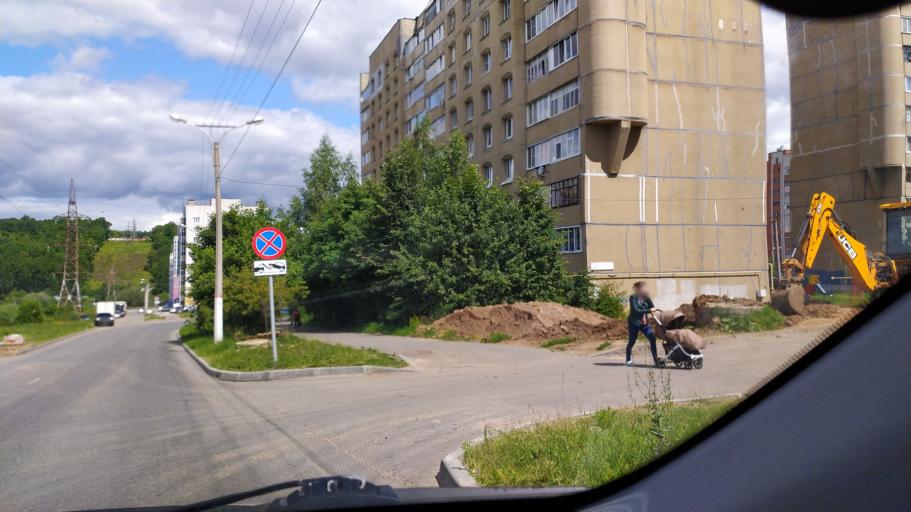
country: RU
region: Chuvashia
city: Novyye Lapsary
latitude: 56.1204
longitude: 47.1748
